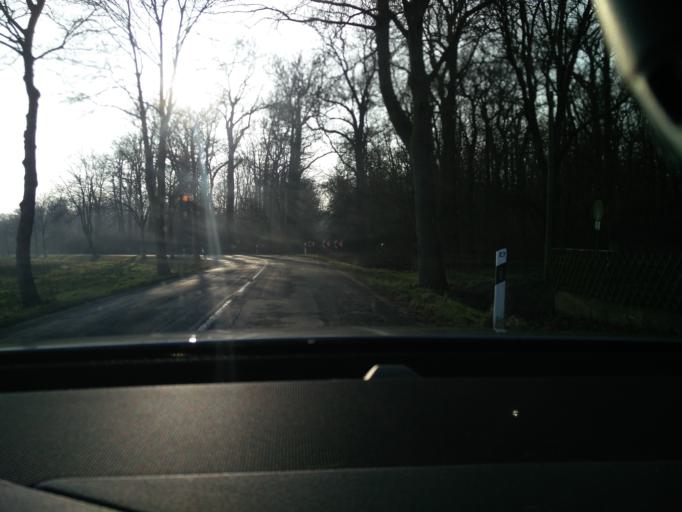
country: DE
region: Lower Saxony
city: Laatzen
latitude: 52.3229
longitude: 9.8504
